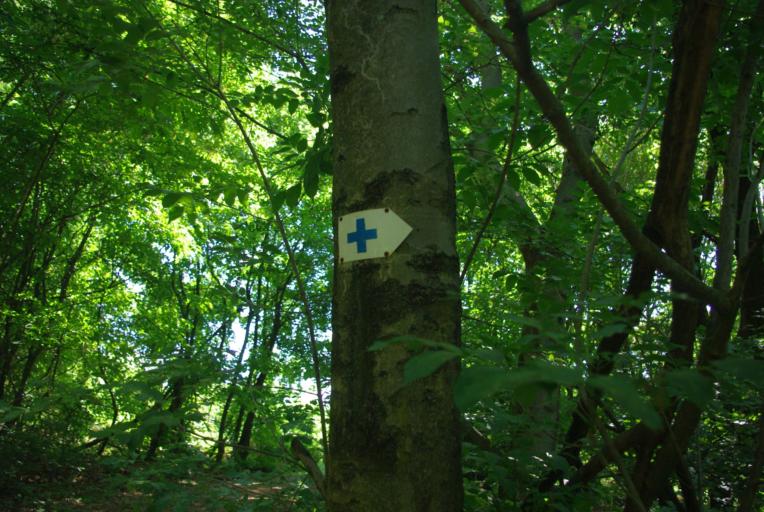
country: HU
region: Pest
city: Pilisborosjeno
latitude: 47.6027
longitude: 18.9785
